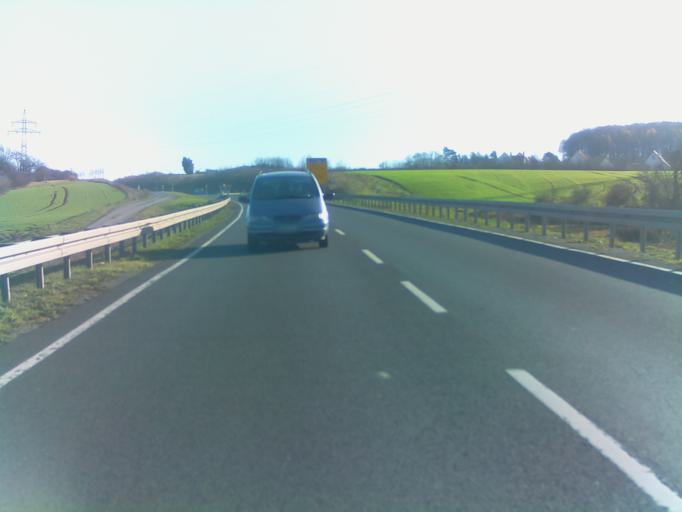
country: DE
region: Bavaria
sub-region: Regierungsbezirk Unterfranken
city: Heustreu
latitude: 50.3366
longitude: 10.2472
